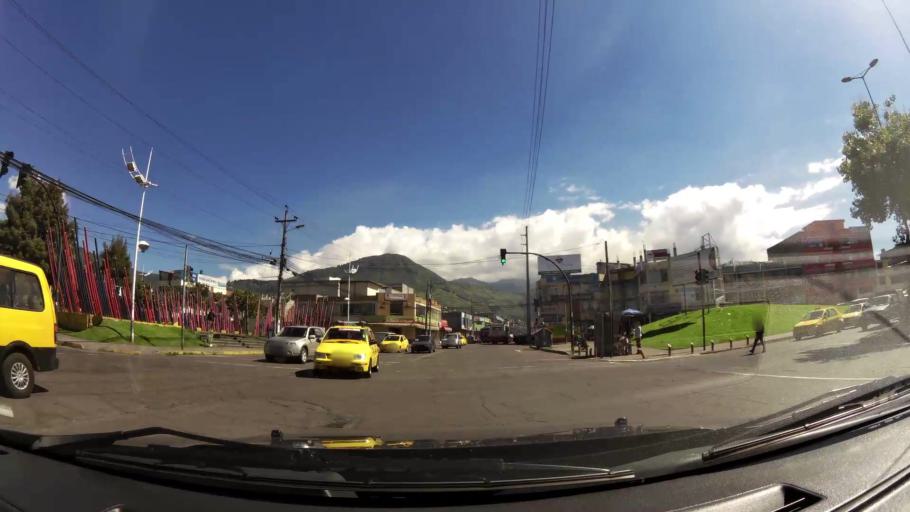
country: EC
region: Pichincha
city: Quito
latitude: -0.2628
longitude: -78.5380
